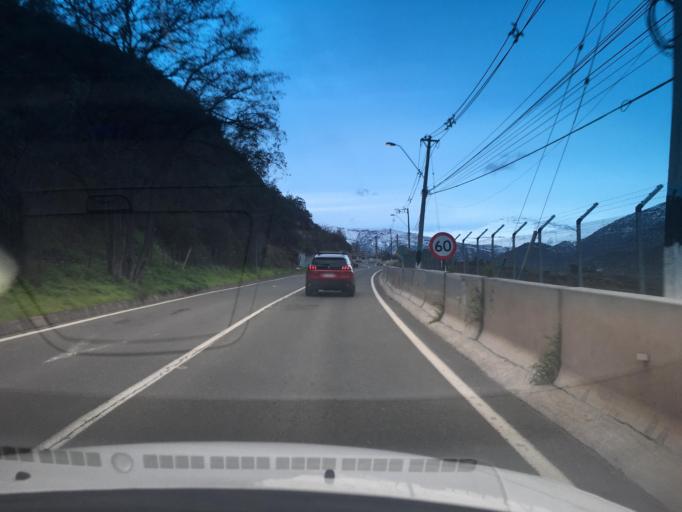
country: CL
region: Santiago Metropolitan
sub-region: Provincia de Cordillera
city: Puente Alto
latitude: -33.5781
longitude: -70.4208
